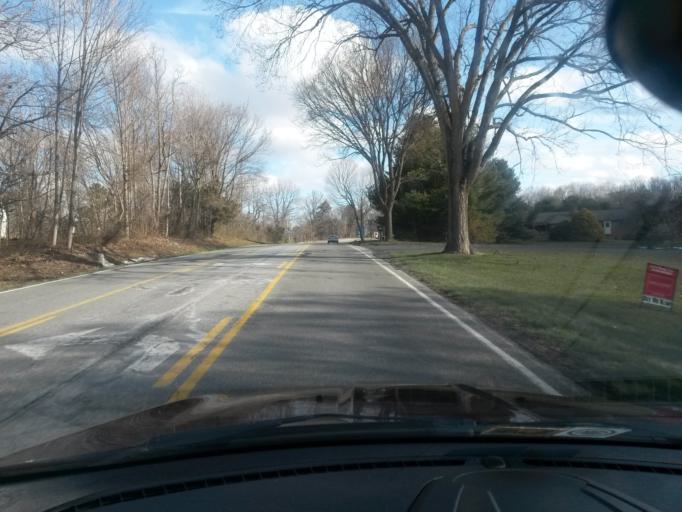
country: US
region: Virginia
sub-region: Augusta County
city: Jolivue
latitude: 38.0762
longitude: -79.1004
